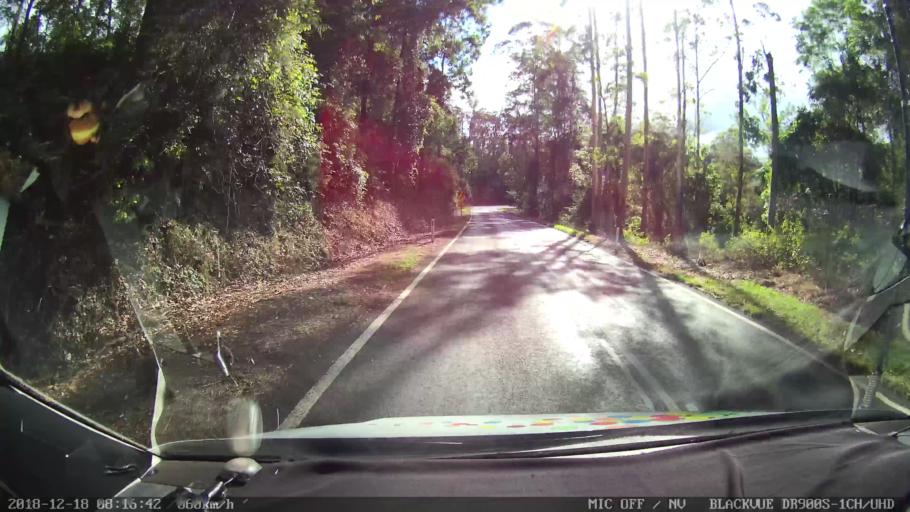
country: AU
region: New South Wales
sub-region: Kyogle
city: Kyogle
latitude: -28.3366
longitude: 152.6956
